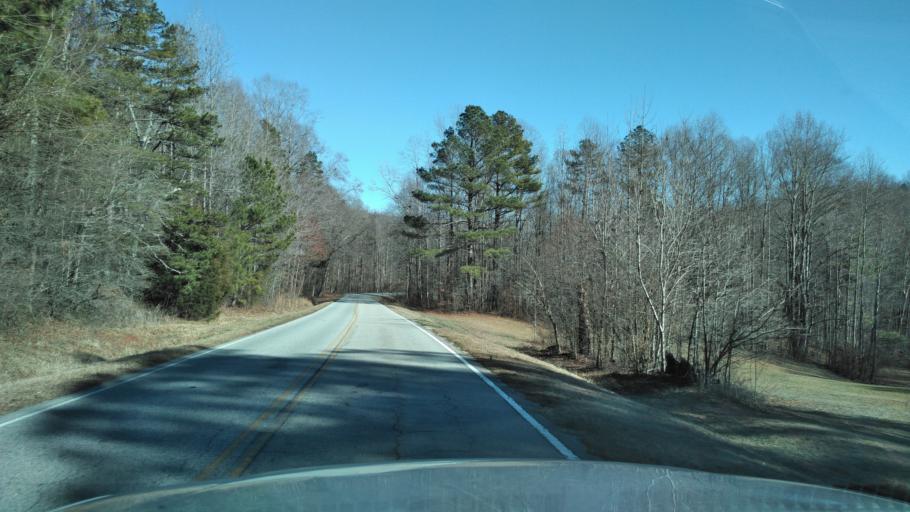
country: US
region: Georgia
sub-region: Hall County
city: Lula
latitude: 34.3184
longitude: -83.6920
